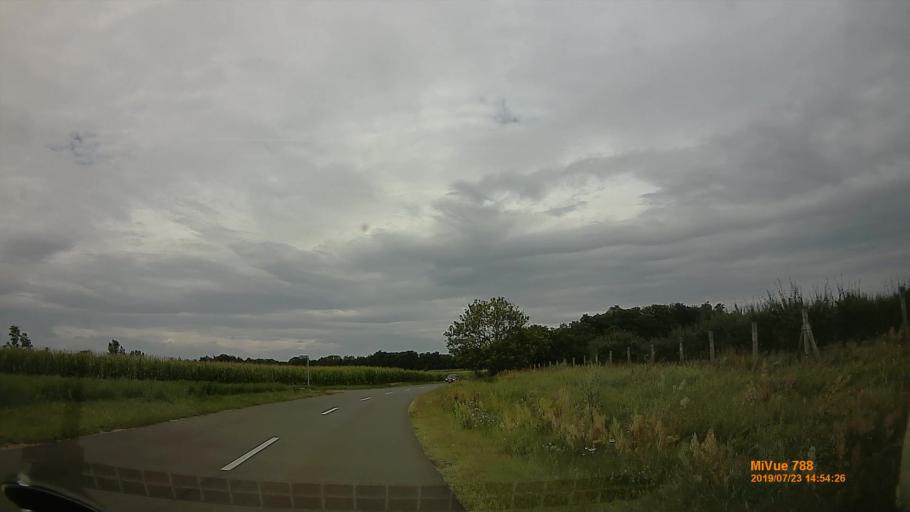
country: HU
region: Szabolcs-Szatmar-Bereg
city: Kalmanhaza
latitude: 47.8856
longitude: 21.6504
